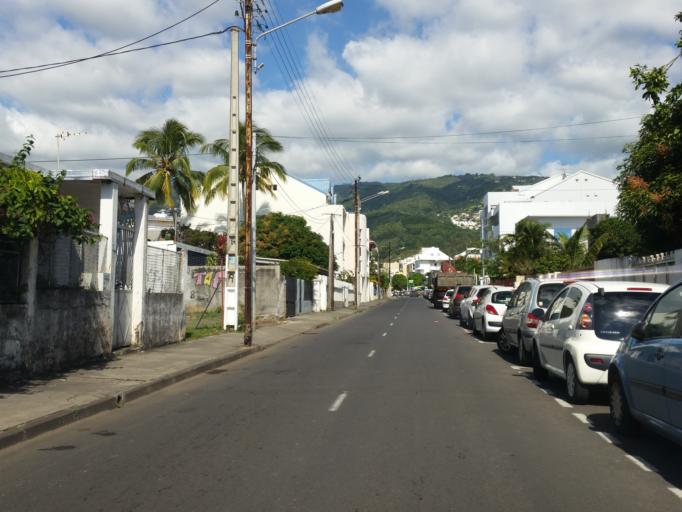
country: RE
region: Reunion
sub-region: Reunion
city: Saint-Denis
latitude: -20.8854
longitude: 55.4593
